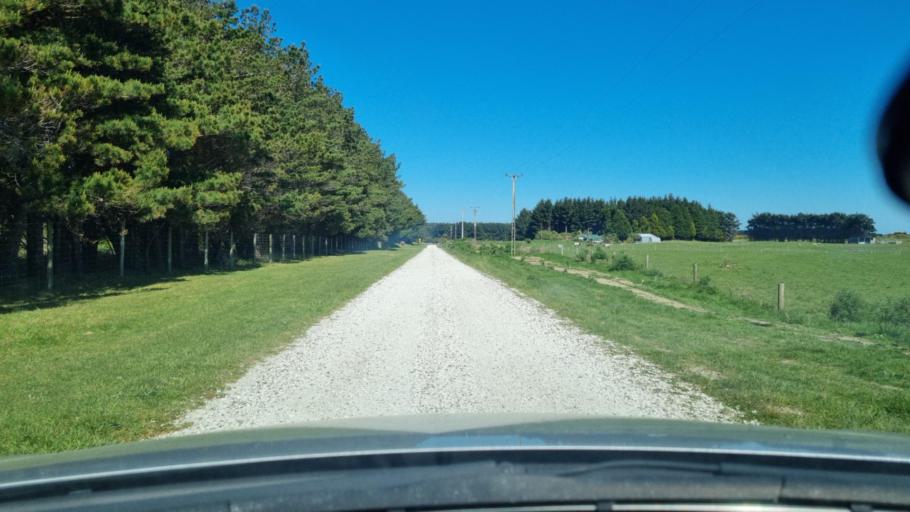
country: NZ
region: Southland
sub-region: Invercargill City
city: Invercargill
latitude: -46.4560
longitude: 168.2737
